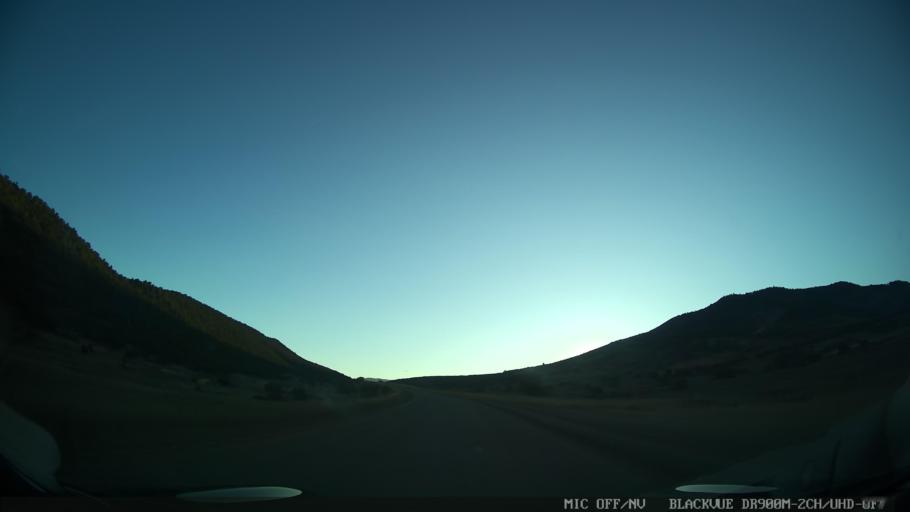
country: US
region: Colorado
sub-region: Grand County
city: Kremmling
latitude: 39.9097
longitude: -106.5761
